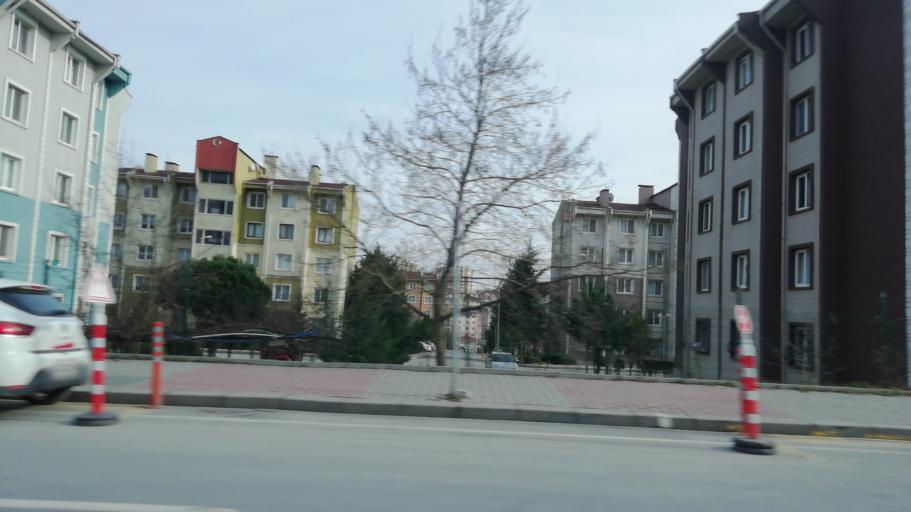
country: TR
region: Istanbul
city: Basaksehir
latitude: 41.1123
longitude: 28.7972
